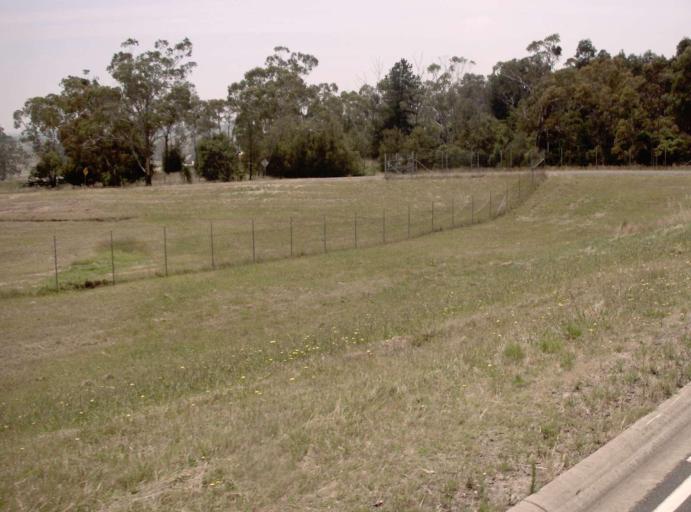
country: AU
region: Victoria
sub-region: Latrobe
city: Traralgon
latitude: -38.2527
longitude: 146.5925
